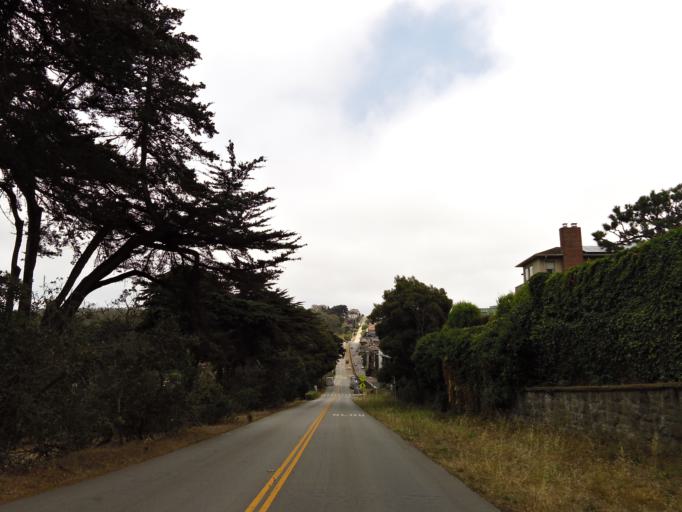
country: US
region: California
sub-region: San Francisco County
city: San Francisco
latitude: 37.7904
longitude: -122.4556
